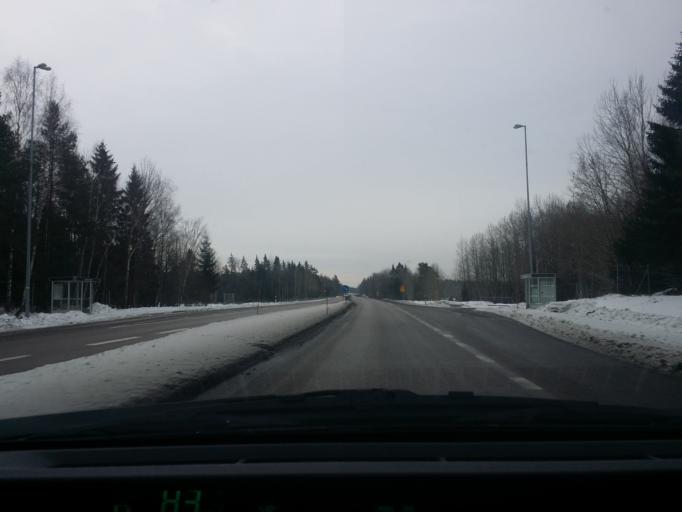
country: SE
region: Vaestra Goetaland
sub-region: Skovde Kommun
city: Stopen
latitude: 58.5273
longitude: 13.8200
